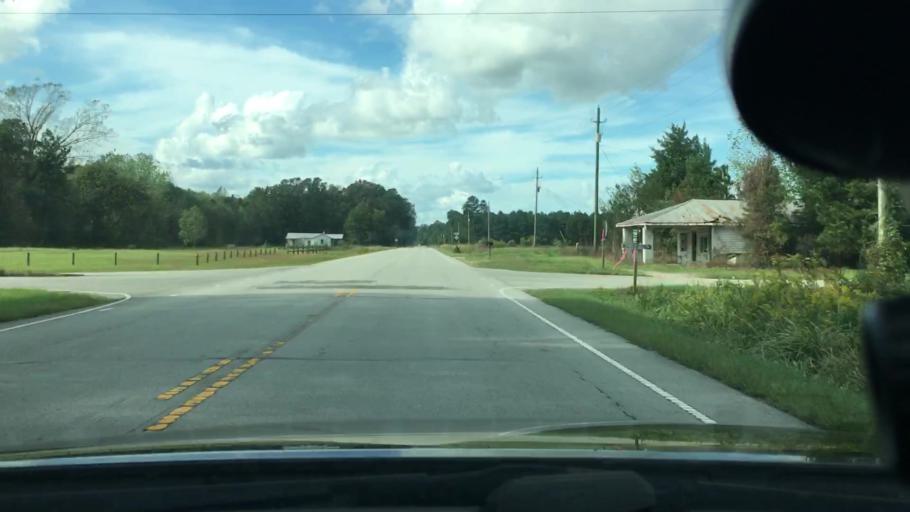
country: US
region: North Carolina
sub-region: Craven County
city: Vanceboro
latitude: 35.4006
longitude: -77.2380
